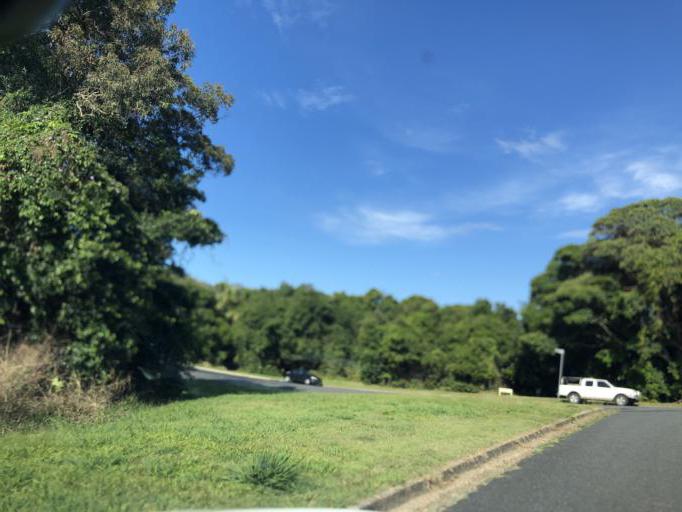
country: AU
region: New South Wales
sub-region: Coffs Harbour
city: Moonee Beach
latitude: -30.2365
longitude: 153.1507
